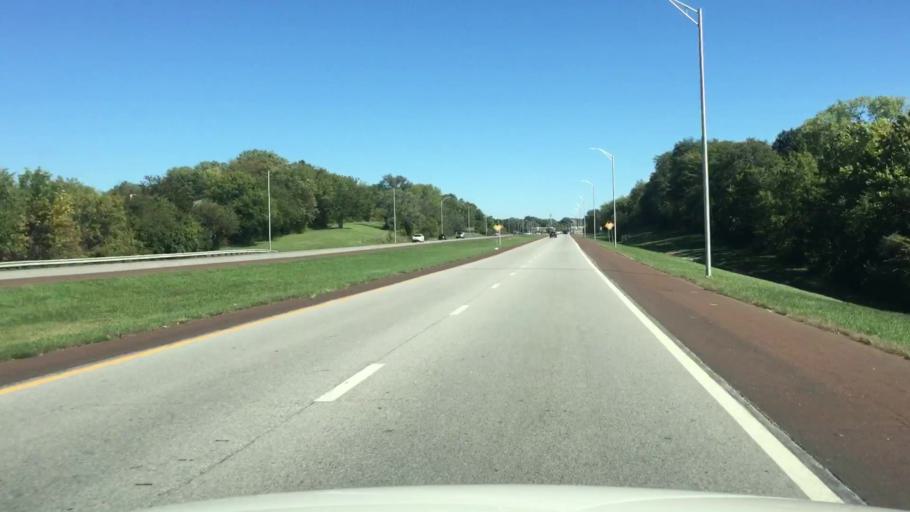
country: US
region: Kansas
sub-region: Johnson County
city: Shawnee
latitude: 39.0104
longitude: -94.7524
